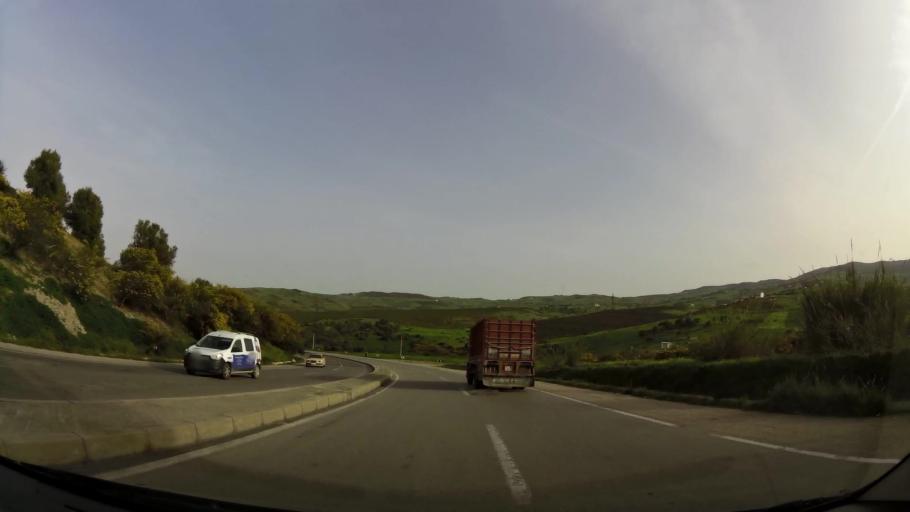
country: MA
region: Tanger-Tetouan
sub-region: Tetouan
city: Saddina
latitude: 35.5494
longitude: -5.5427
